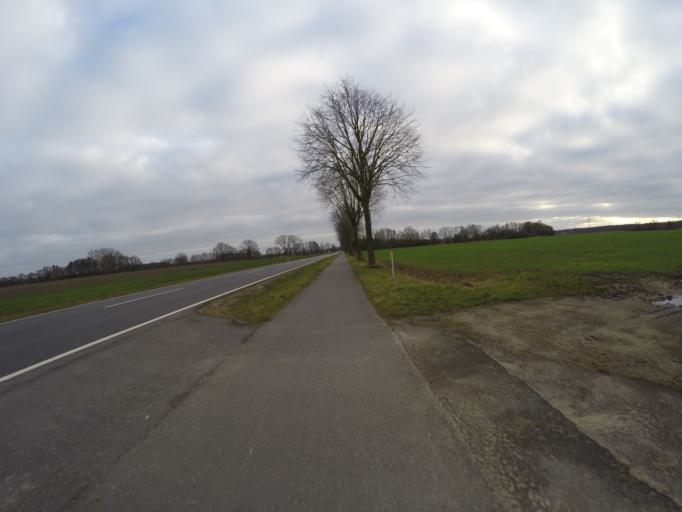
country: DE
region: Schleswig-Holstein
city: Alveslohe
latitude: 53.7689
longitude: 9.9068
